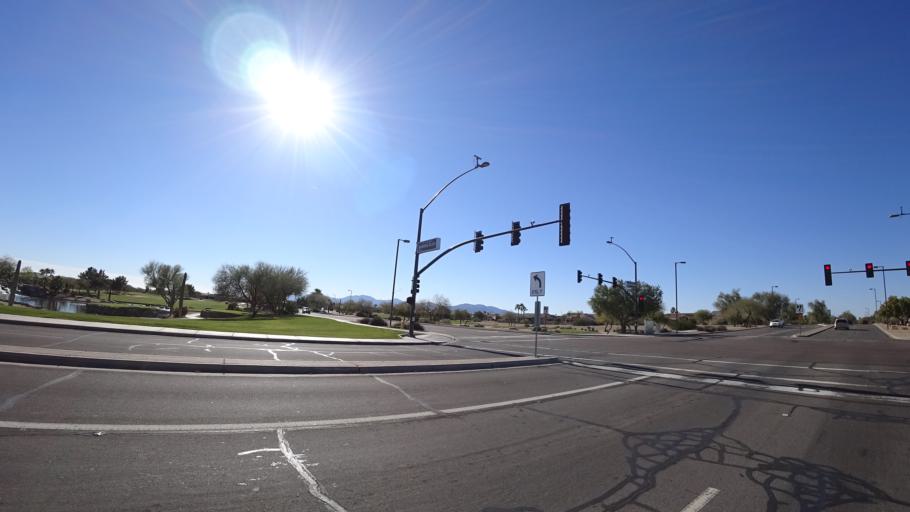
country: US
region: Arizona
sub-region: Maricopa County
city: Sun City West
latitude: 33.6660
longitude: -112.3928
